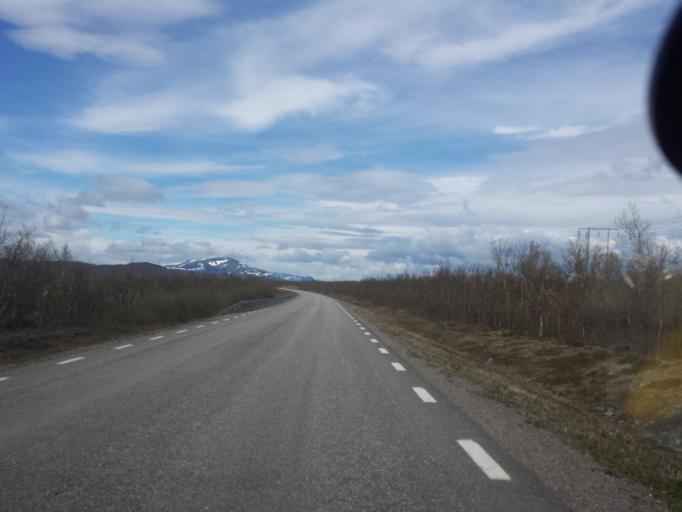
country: SE
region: Norrbotten
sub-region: Kiruna Kommun
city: Kiruna
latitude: 68.0501
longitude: 19.8304
